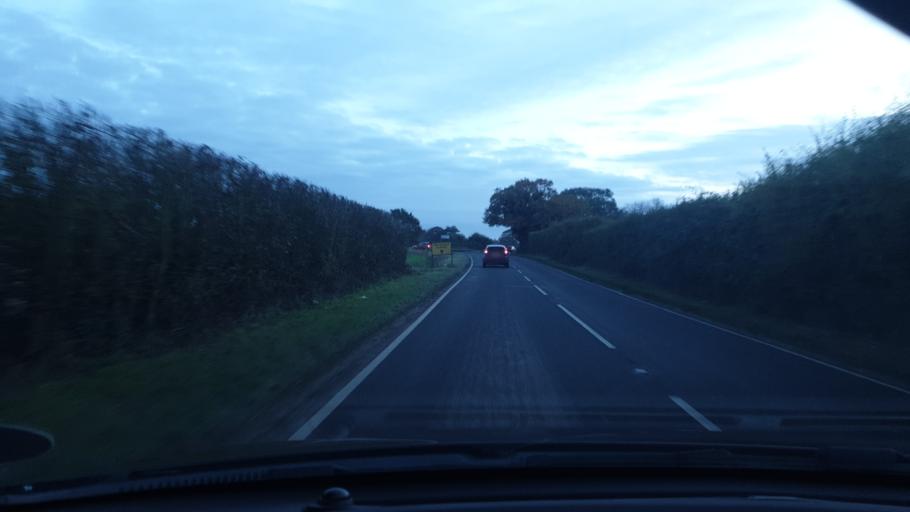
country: GB
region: England
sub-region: Essex
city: Little Clacton
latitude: 51.8660
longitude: 1.1752
